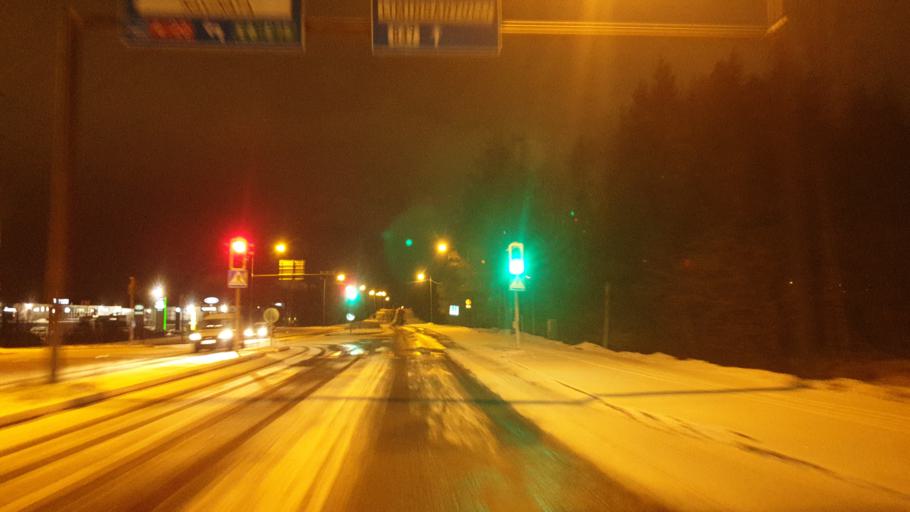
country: FI
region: Northern Ostrobothnia
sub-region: Oulu
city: Oulu
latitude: 64.9855
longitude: 25.4758
